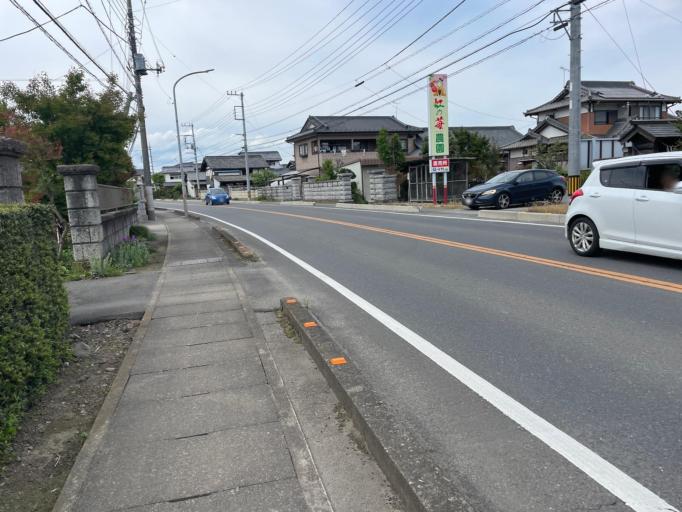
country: JP
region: Tochigi
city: Mibu
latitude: 36.4563
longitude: 139.7742
